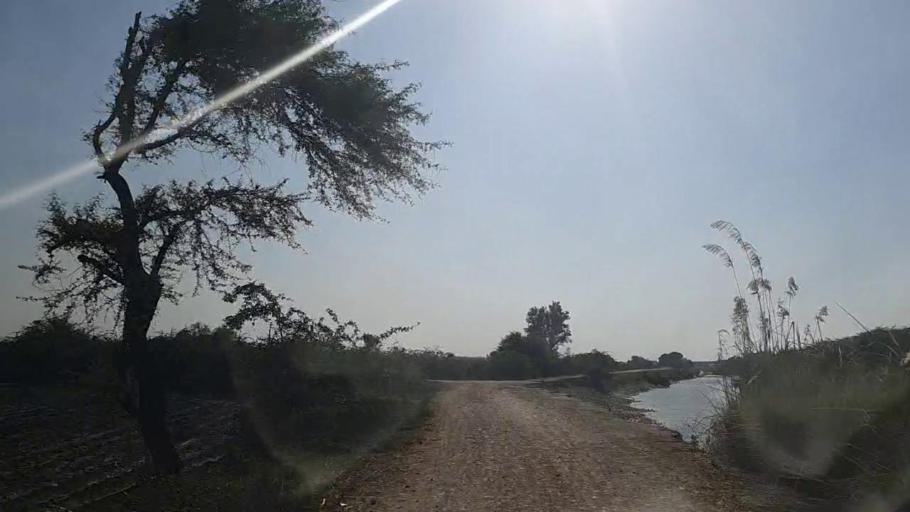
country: PK
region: Sindh
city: Mirpur Batoro
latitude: 24.6503
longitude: 68.1775
